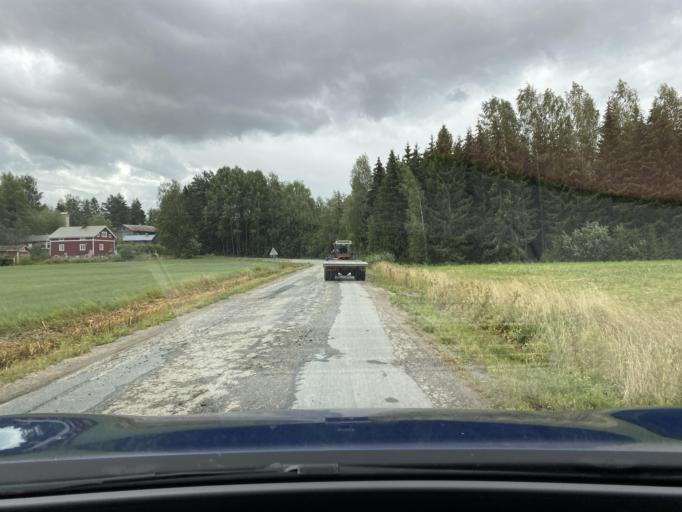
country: FI
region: Pirkanmaa
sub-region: Lounais-Pirkanmaa
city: Punkalaidun
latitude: 61.1698
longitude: 23.1787
